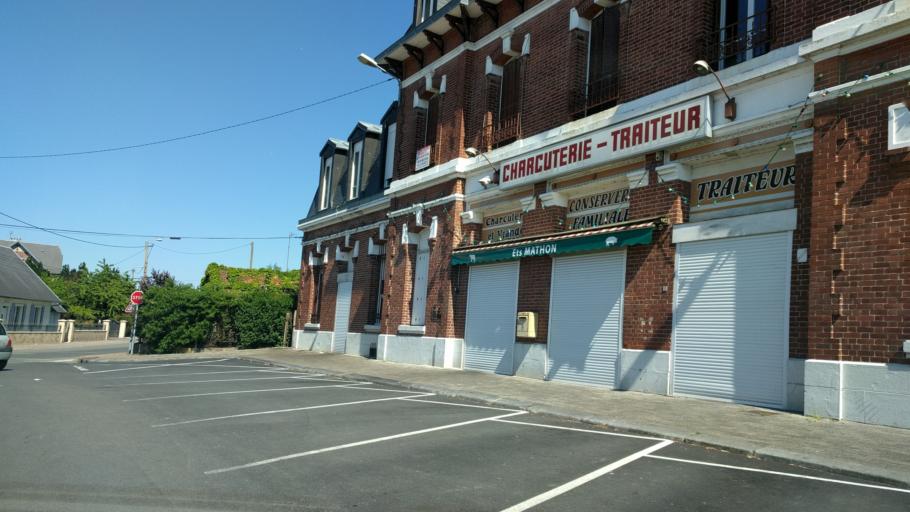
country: FR
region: Picardie
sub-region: Departement de la Somme
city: Peronne
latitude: 49.9276
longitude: 2.9406
